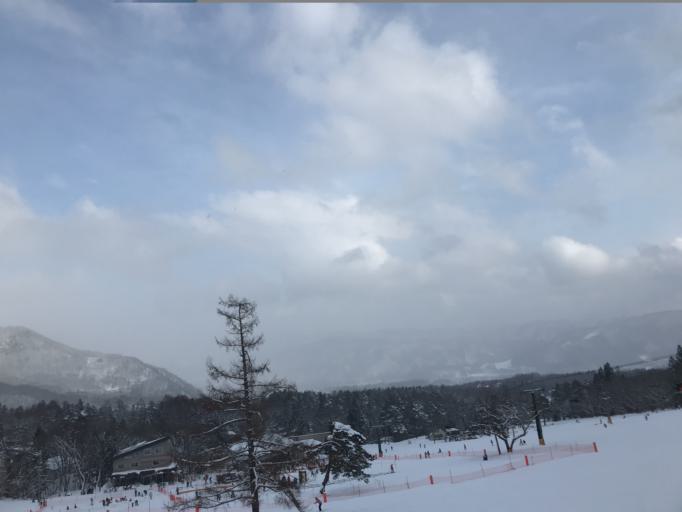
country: JP
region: Nagano
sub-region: Kitaazumi Gun
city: Hakuba
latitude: 36.7111
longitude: 137.8282
